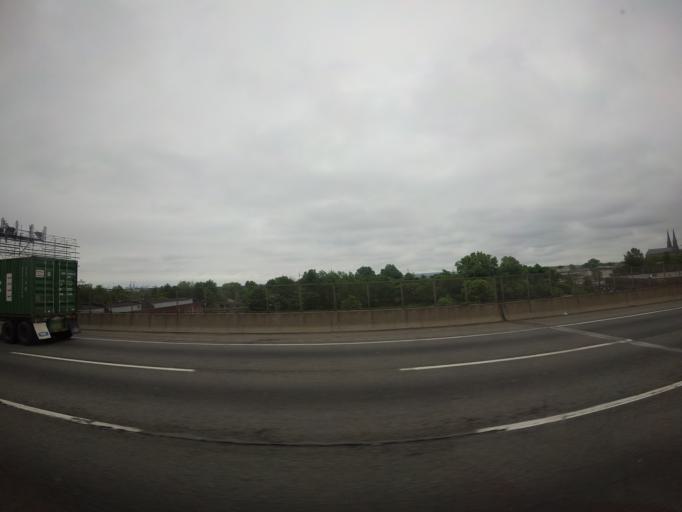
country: US
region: New Jersey
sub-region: Union County
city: Elizabeth
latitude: 40.6581
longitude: -74.1869
